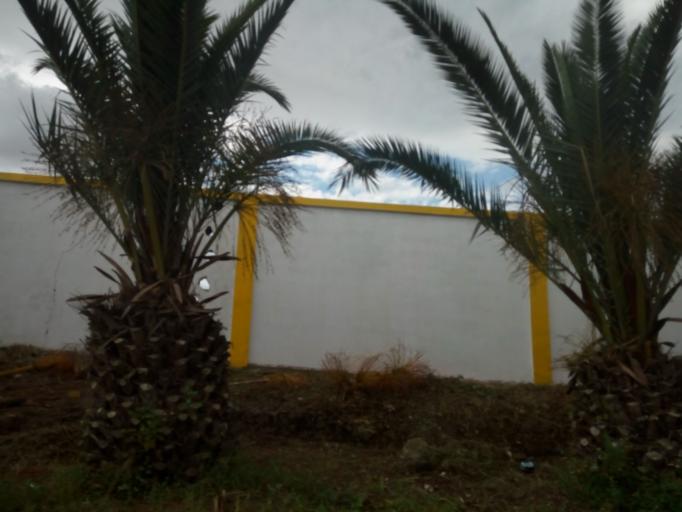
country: DZ
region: Tipaza
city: Douera
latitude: 36.6256
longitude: 2.9433
